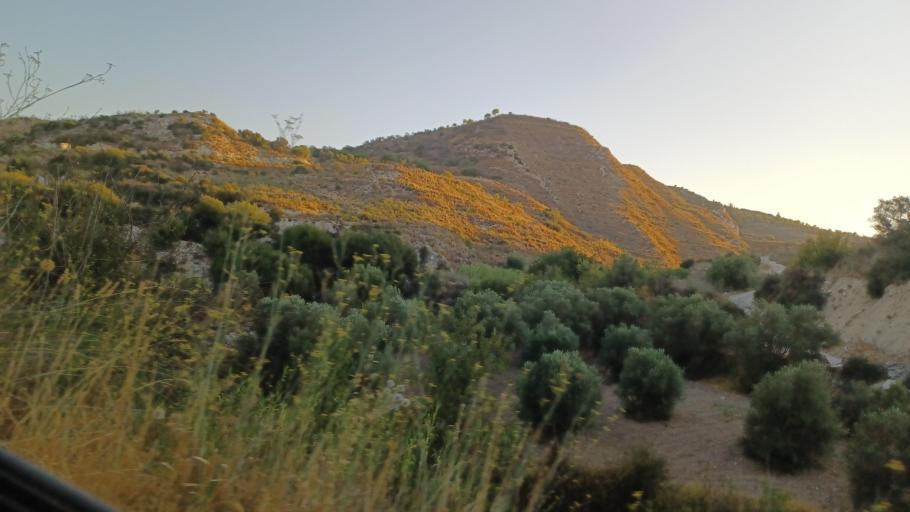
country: CY
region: Pafos
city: Tala
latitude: 34.9051
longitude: 32.5108
